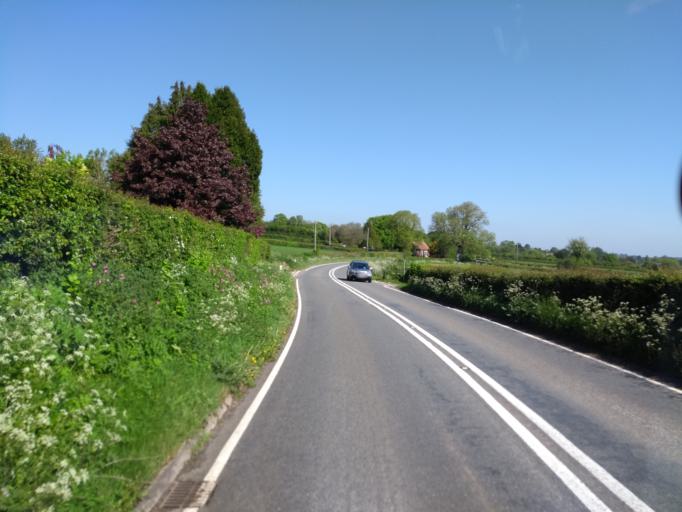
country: GB
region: England
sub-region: Somerset
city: Chard
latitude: 50.8404
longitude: -2.9598
